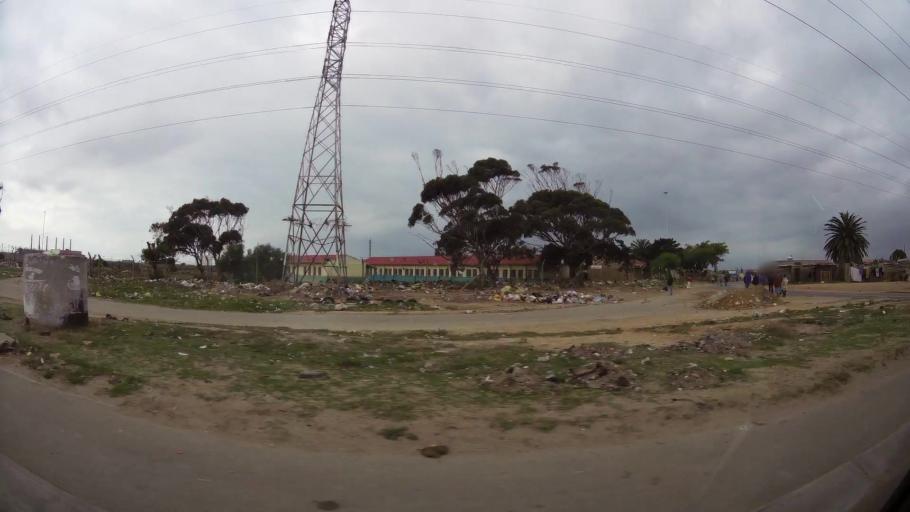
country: ZA
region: Eastern Cape
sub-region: Nelson Mandela Bay Metropolitan Municipality
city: Port Elizabeth
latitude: -33.8800
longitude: 25.5846
